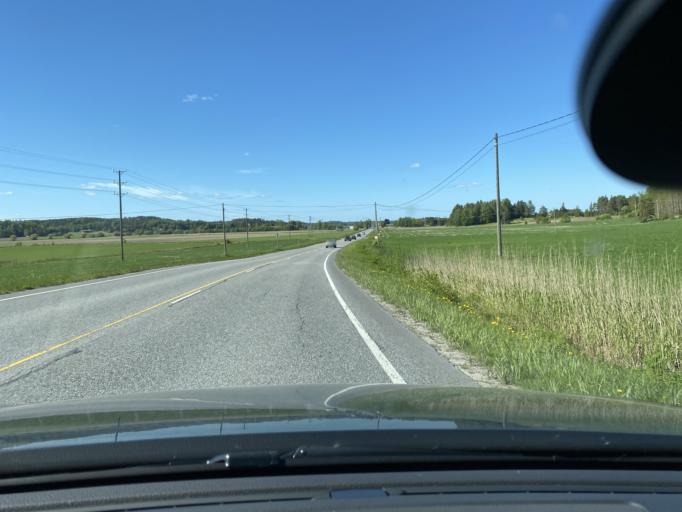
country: FI
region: Varsinais-Suomi
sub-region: Turku
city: Paimio
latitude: 60.4116
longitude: 22.6656
